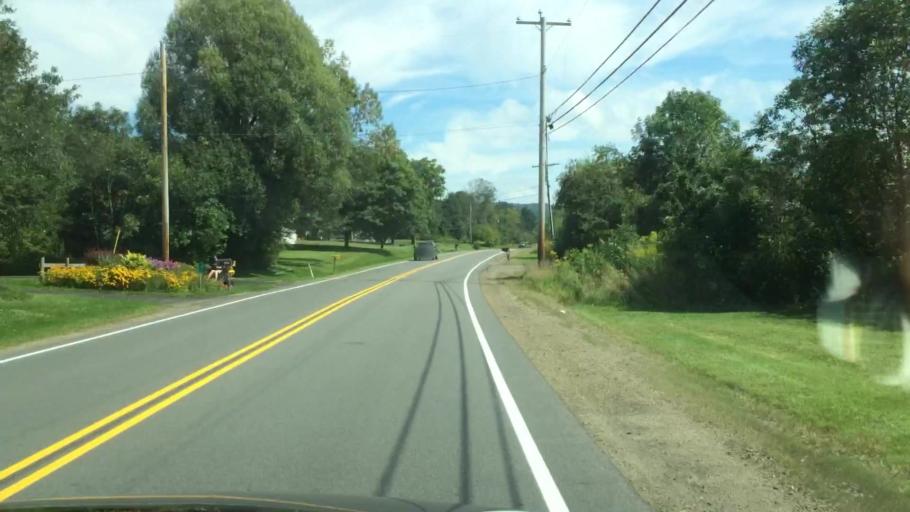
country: US
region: Pennsylvania
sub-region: McKean County
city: Bradford
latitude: 41.9121
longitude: -78.6377
